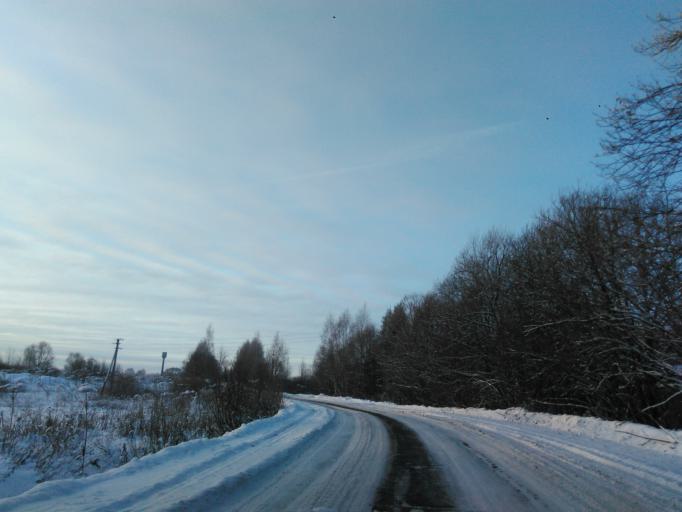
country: RU
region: Tverskaya
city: Zavidovo
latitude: 56.6345
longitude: 36.6216
